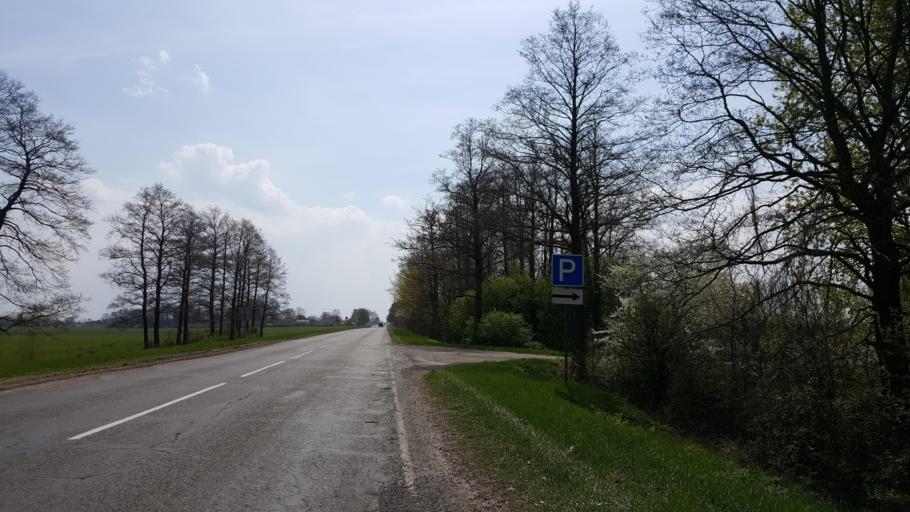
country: BY
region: Brest
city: Zhabinka
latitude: 52.2341
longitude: 23.9819
